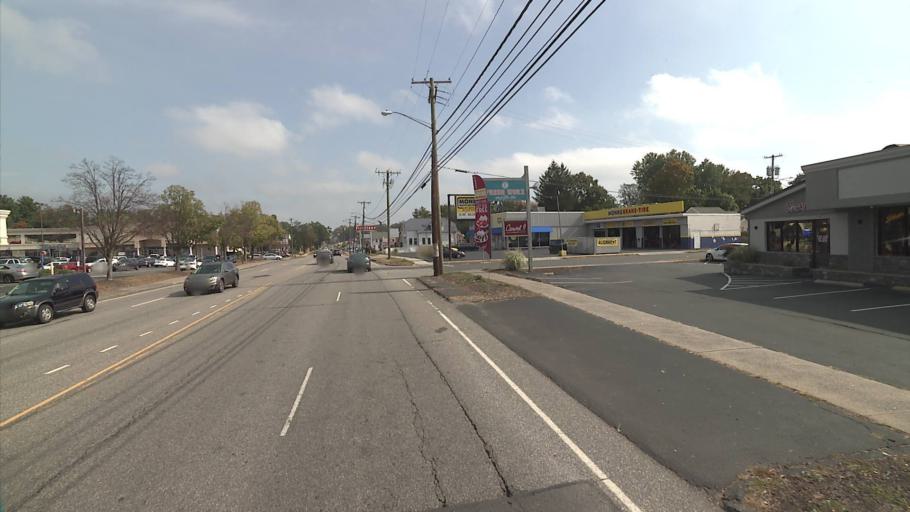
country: US
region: Connecticut
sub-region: Hartford County
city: Bristol
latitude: 41.6908
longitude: -72.9222
